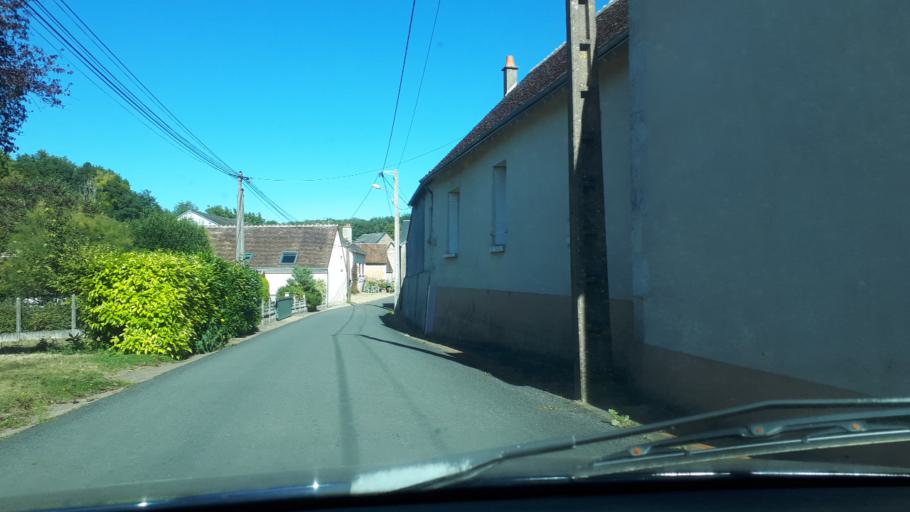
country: FR
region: Centre
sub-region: Departement du Loir-et-Cher
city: Villiers-sur-Loir
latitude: 47.8042
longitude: 1.0029
